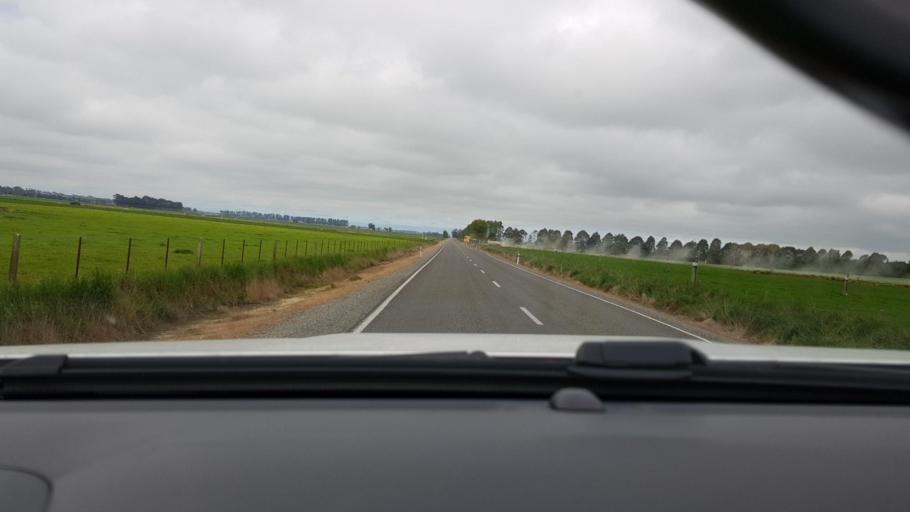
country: NZ
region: Otago
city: Oamaru
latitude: -44.9649
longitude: 170.9345
